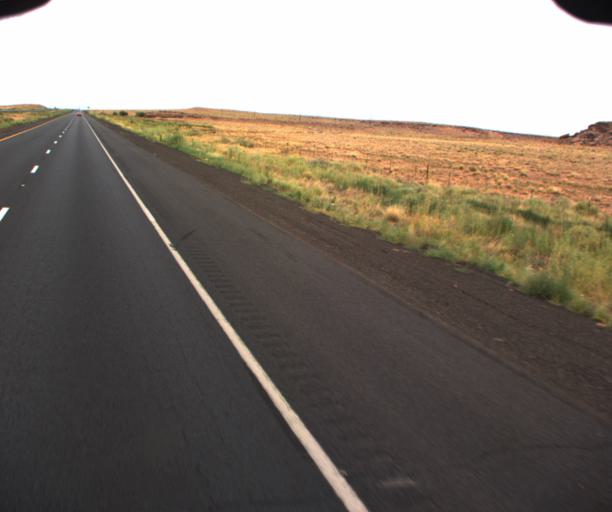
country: US
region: Arizona
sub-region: Navajo County
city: Joseph City
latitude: 34.9723
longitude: -110.4896
